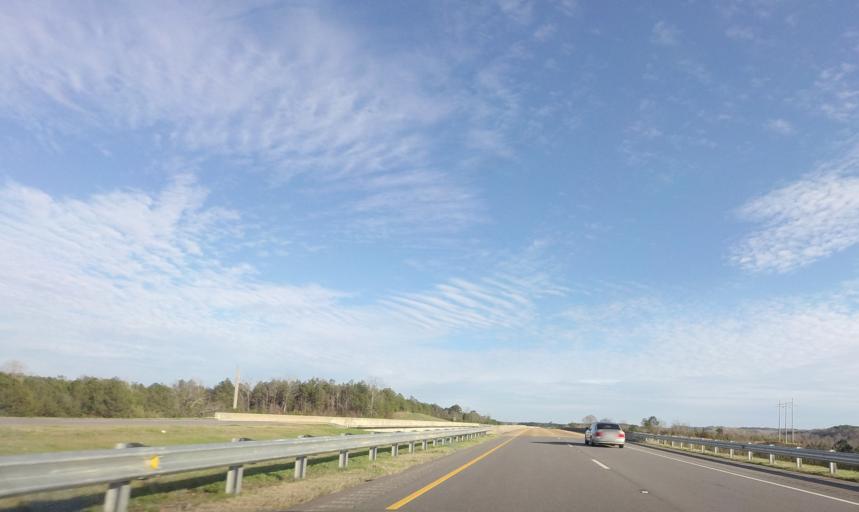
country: US
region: Alabama
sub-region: Walker County
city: Jasper
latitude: 33.8102
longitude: -87.2950
